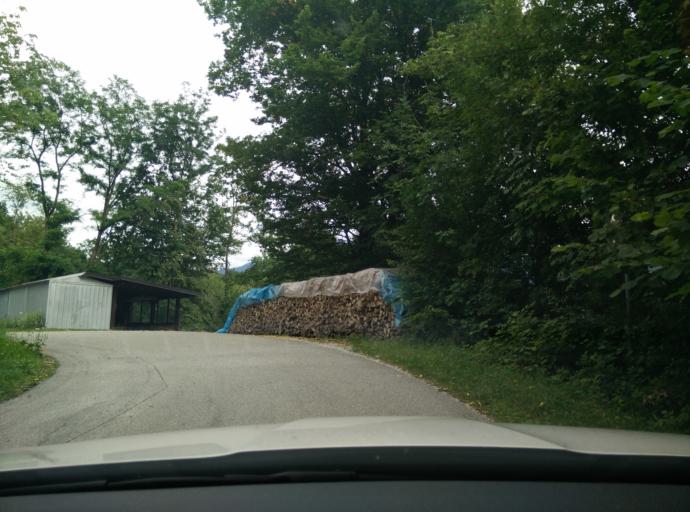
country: SI
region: Bovec
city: Bovec
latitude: 46.3368
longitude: 13.5228
